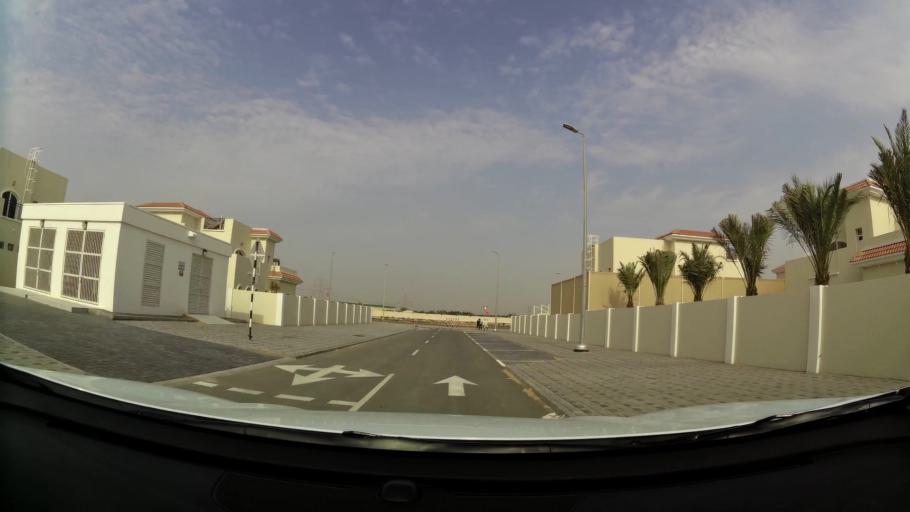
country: AE
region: Abu Dhabi
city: Abu Dhabi
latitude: 24.6720
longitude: 54.7483
